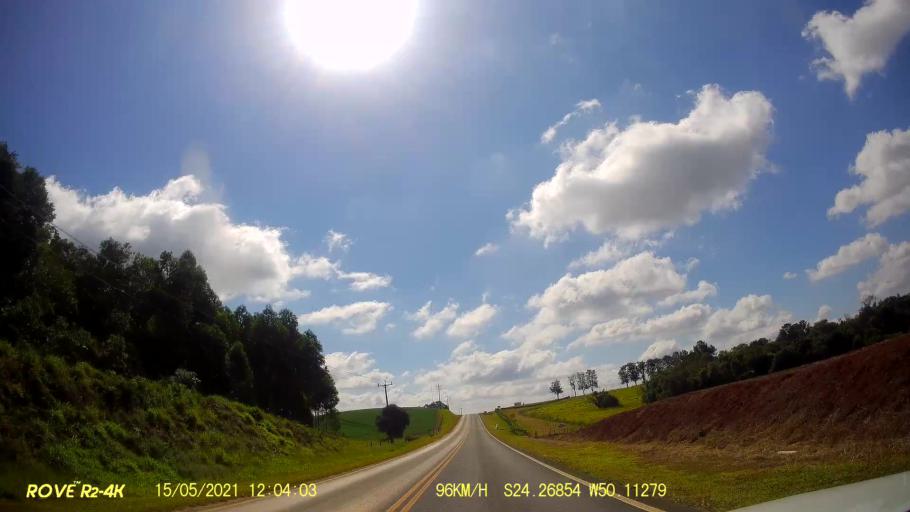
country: BR
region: Parana
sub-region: Pirai Do Sul
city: Pirai do Sul
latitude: -24.2685
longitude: -50.1131
